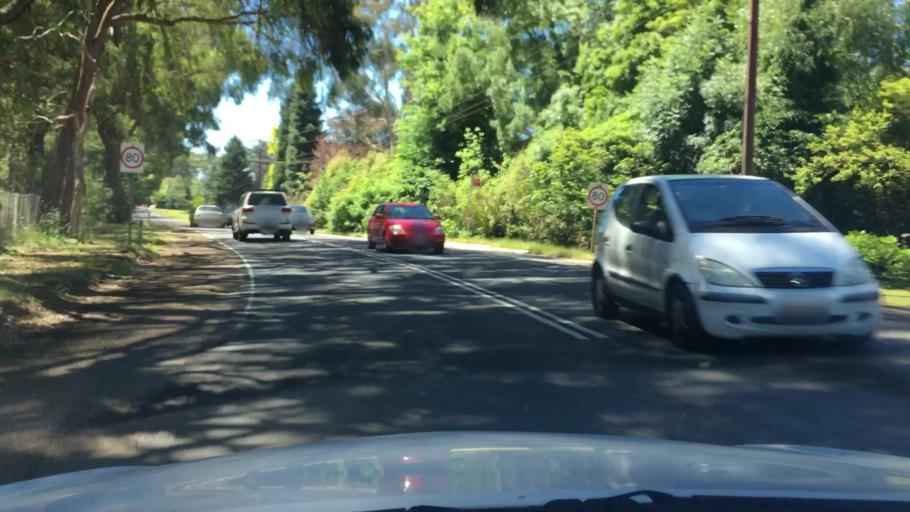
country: AU
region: Victoria
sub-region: Yarra Ranges
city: Monbulk
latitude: -37.8503
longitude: 145.4236
